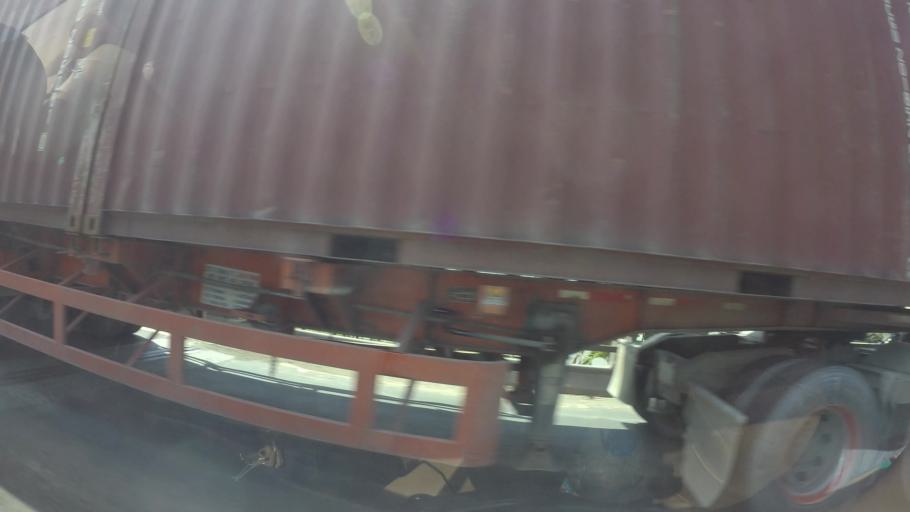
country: VN
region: Ho Chi Minh City
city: Quan Hai
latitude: 10.8040
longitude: 106.7535
